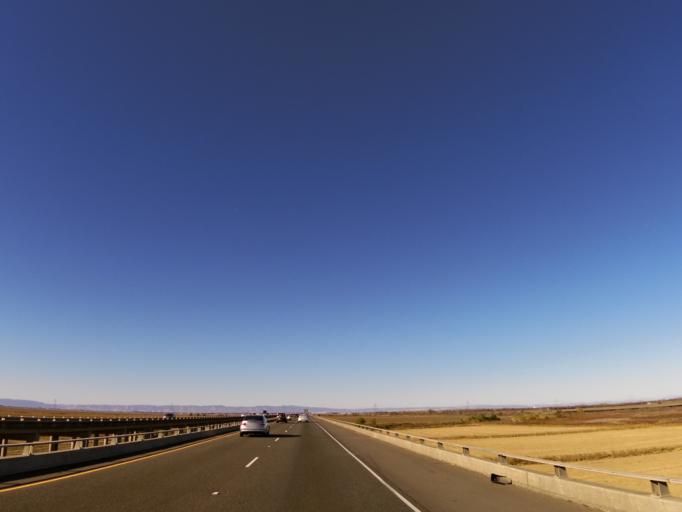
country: US
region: California
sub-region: Yolo County
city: Woodland
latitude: 38.6736
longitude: -121.6506
